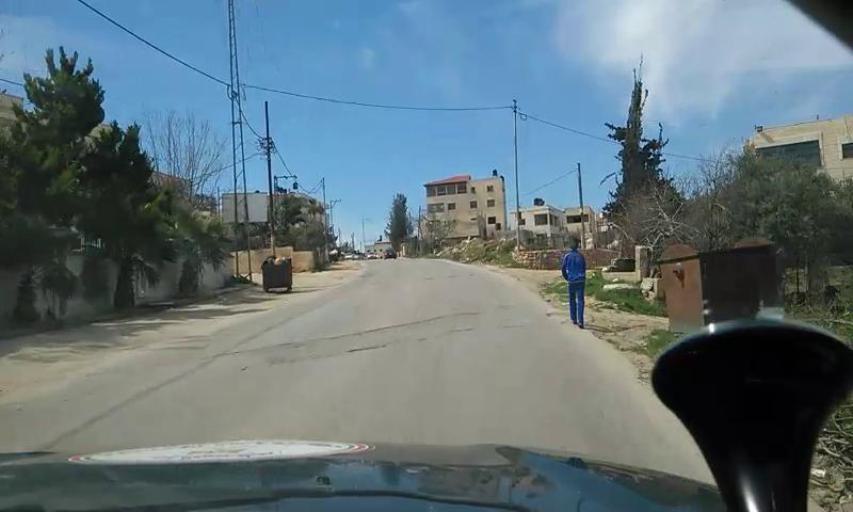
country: PS
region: West Bank
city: Al Jib
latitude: 31.8530
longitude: 35.1875
